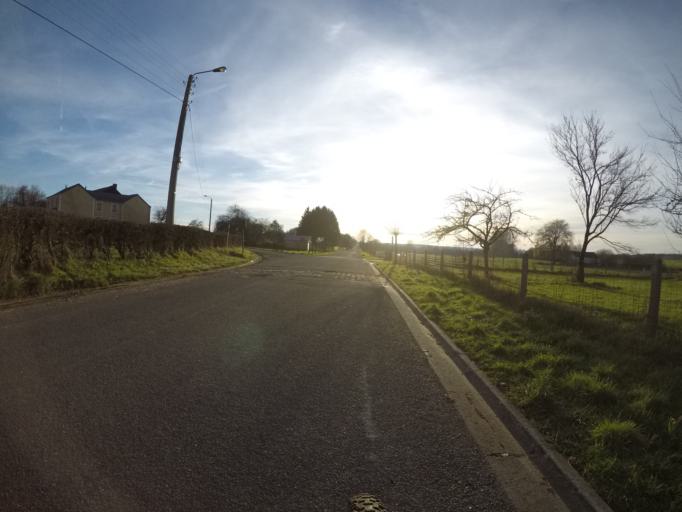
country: BE
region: Wallonia
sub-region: Province du Luxembourg
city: Tintigny
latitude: 49.6744
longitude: 5.4699
